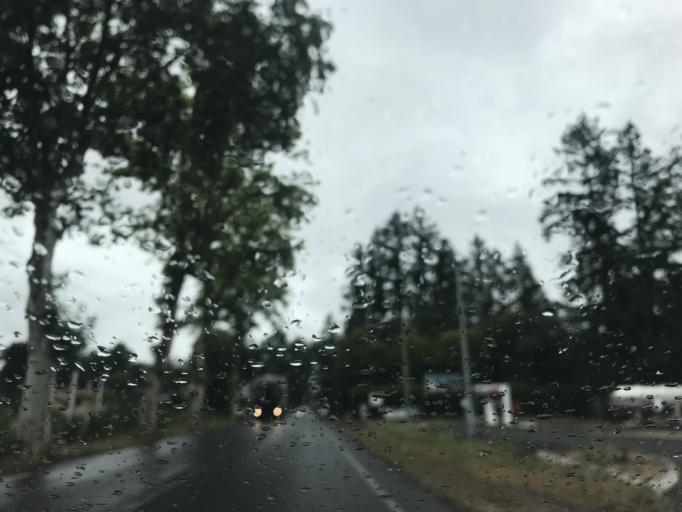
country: FR
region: Auvergne
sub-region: Departement du Puy-de-Dome
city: Ambert
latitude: 45.5577
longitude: 3.7416
